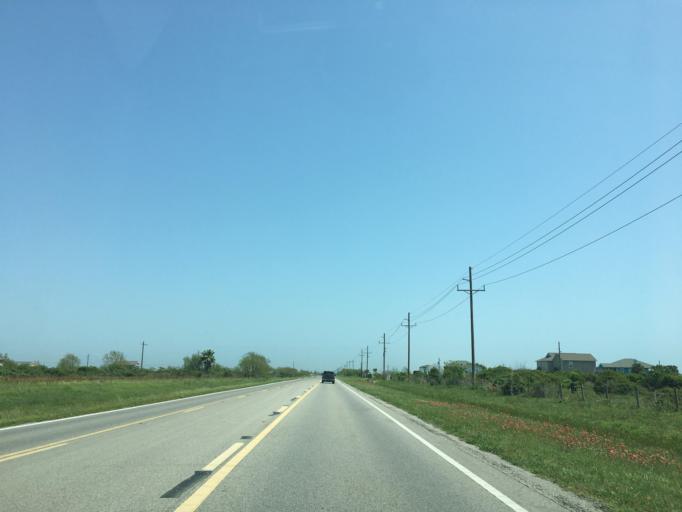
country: US
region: Texas
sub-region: Galveston County
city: Bolivar Peninsula
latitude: 29.4294
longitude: -94.6882
